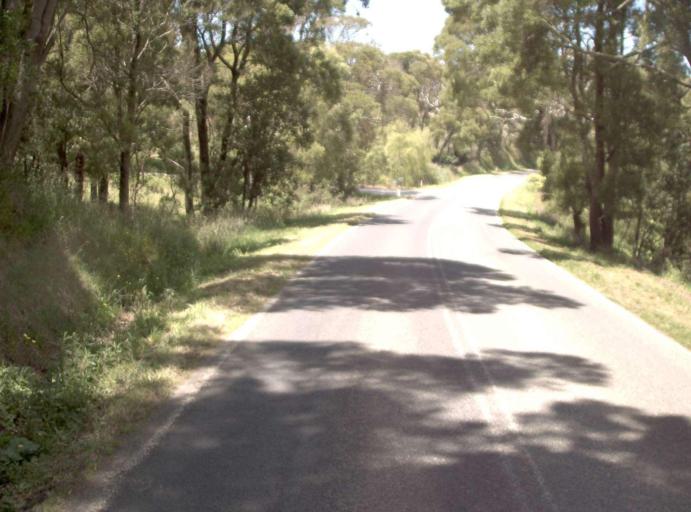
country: AU
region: Victoria
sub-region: Bass Coast
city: North Wonthaggi
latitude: -38.7199
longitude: 146.1199
